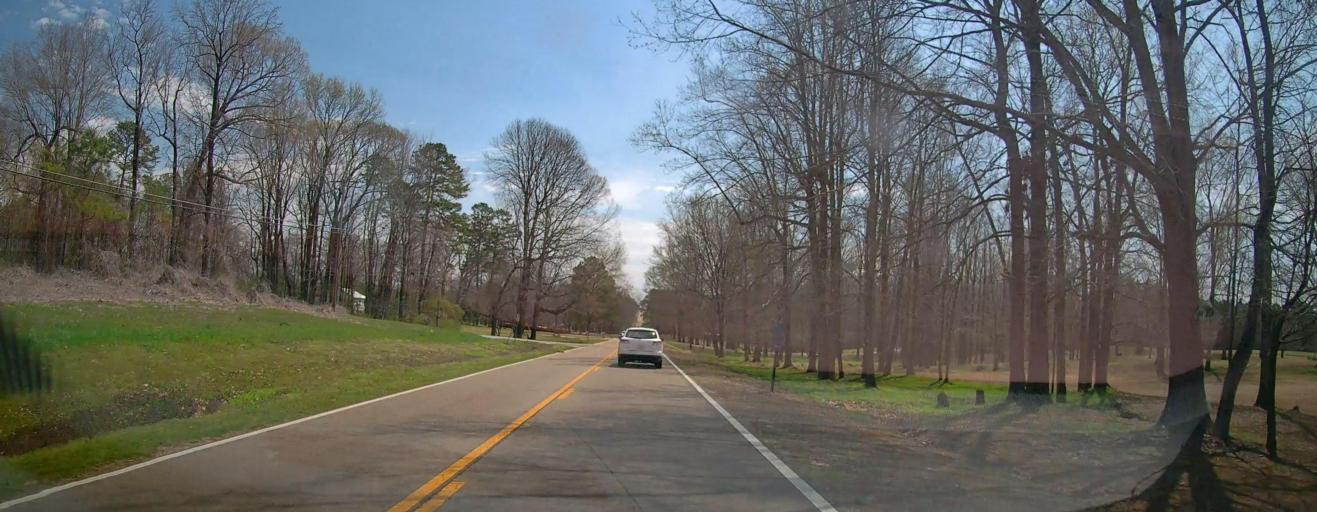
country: US
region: Mississippi
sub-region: Union County
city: New Albany
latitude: 34.4479
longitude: -88.9684
